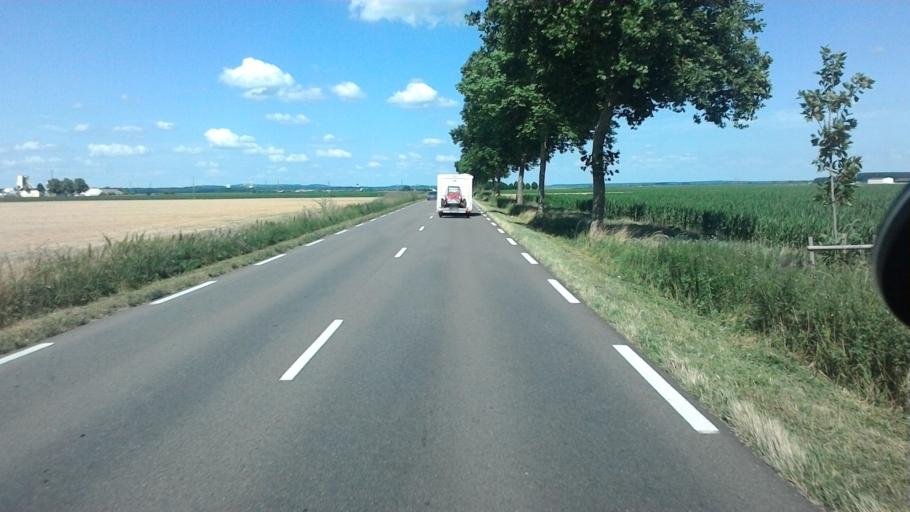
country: FR
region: Franche-Comte
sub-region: Departement du Jura
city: Tavaux
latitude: 47.0113
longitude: 5.3681
